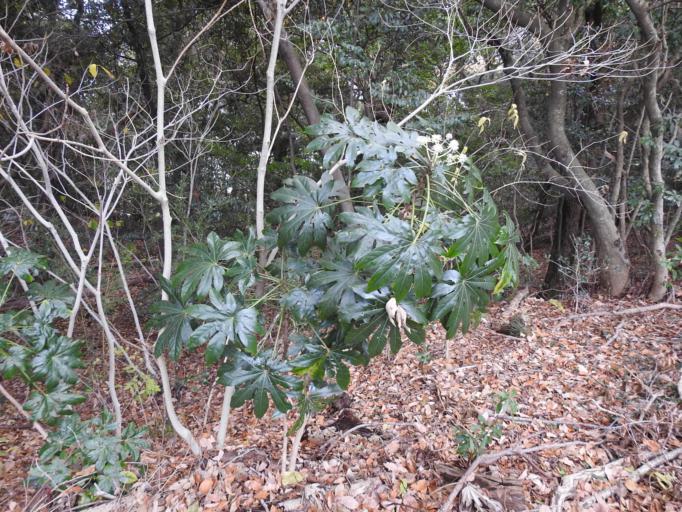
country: JP
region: Fukuoka
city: Fukuoka-shi
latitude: 33.5615
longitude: 130.3991
